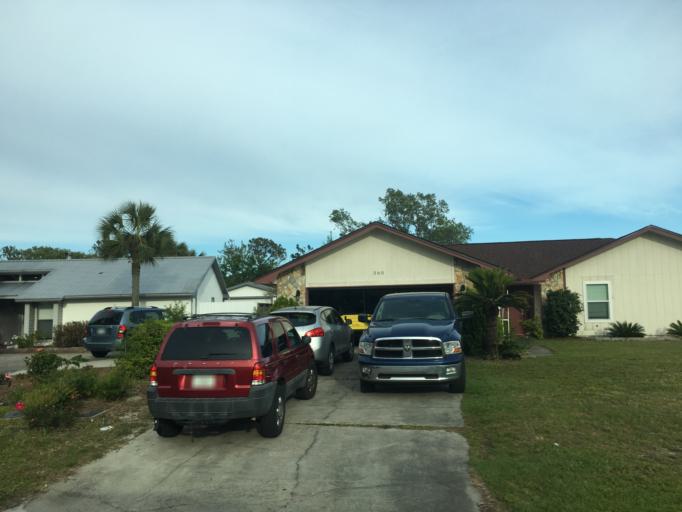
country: US
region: Florida
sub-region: Bay County
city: Lower Grand Lagoon
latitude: 30.1653
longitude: -85.7709
